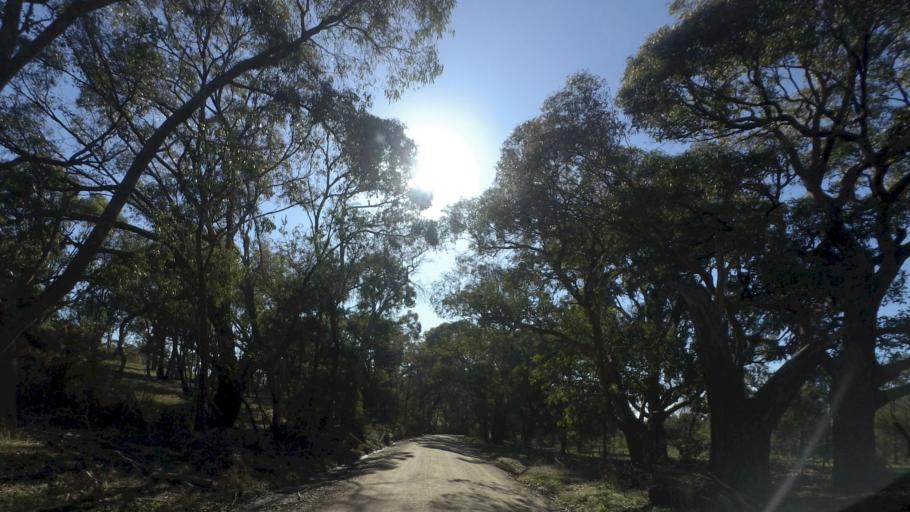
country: AU
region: Victoria
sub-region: Mount Alexander
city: Castlemaine
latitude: -37.1300
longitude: 144.4067
